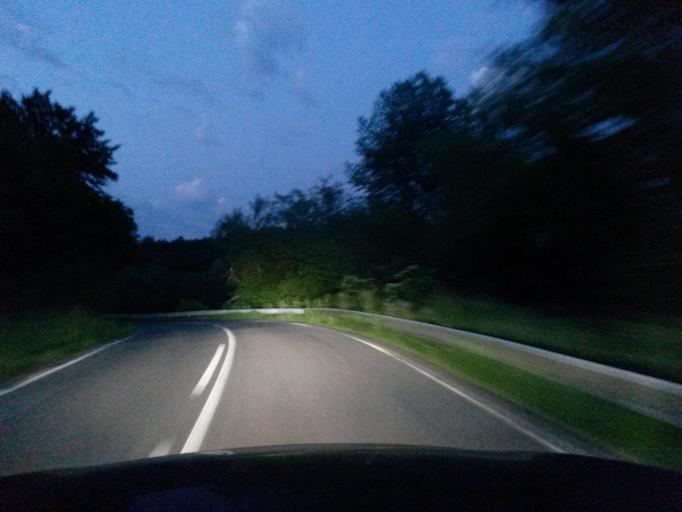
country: UA
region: Zakarpattia
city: Velykyi Bereznyi
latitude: 48.9234
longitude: 22.3247
